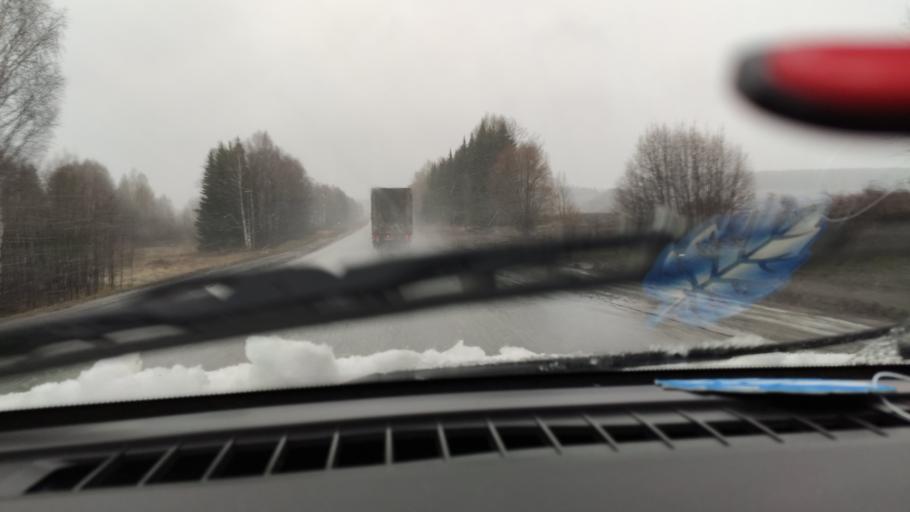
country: RU
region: Perm
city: Kungur
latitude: 57.4632
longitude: 56.7579
